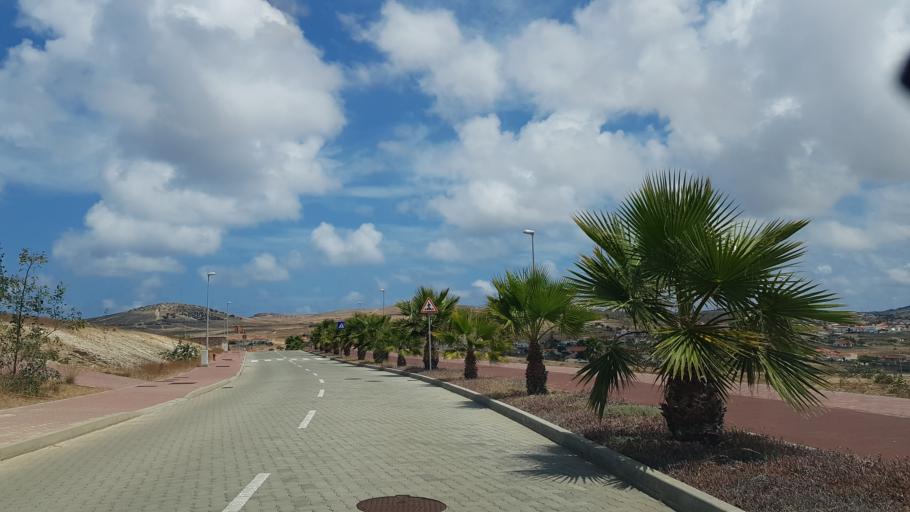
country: PT
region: Madeira
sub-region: Porto Santo
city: Vila de Porto Santo
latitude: 33.0482
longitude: -16.3644
